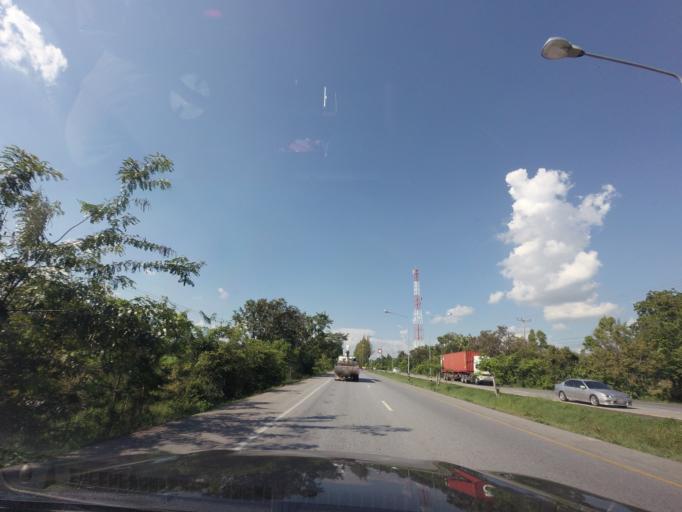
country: TH
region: Nakhon Ratchasima
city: Sida
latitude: 15.5354
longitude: 102.5451
